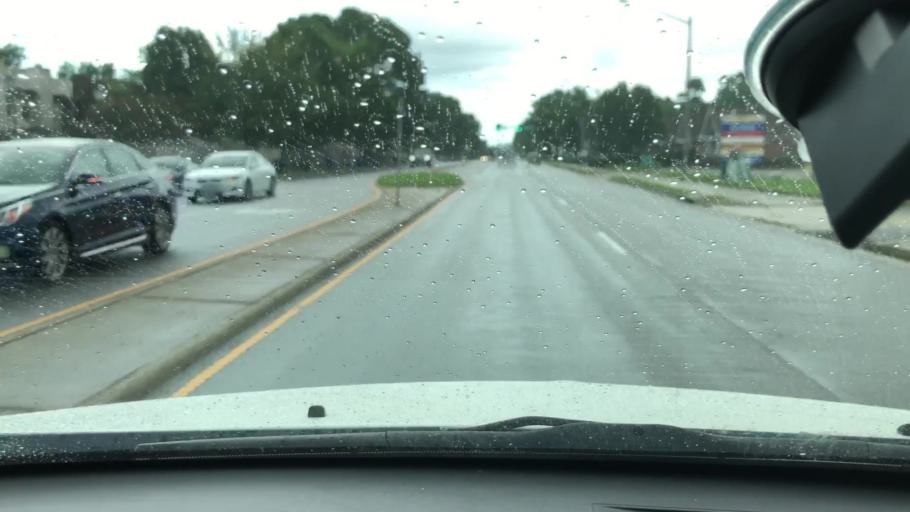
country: US
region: Virginia
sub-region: City of Chesapeake
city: Chesapeake
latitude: 36.8234
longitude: -76.1499
